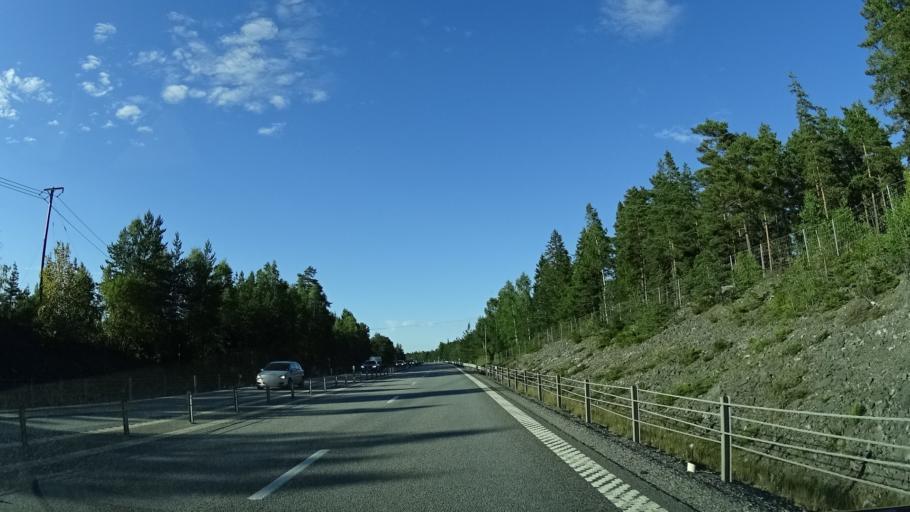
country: SE
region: Stockholm
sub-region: Osterakers Kommun
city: Akersberga
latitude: 59.5954
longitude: 18.2699
